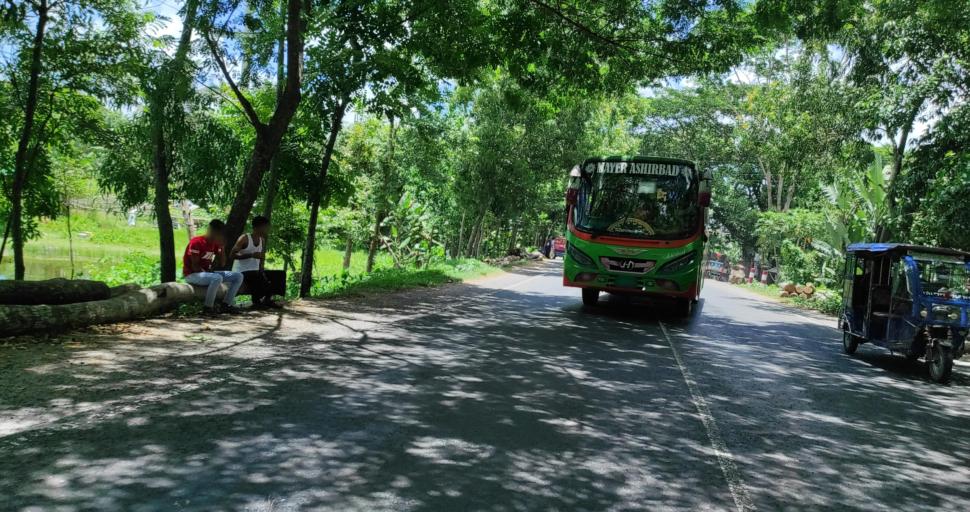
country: BD
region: Barisal
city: Gaurnadi
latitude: 22.8396
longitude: 90.2515
